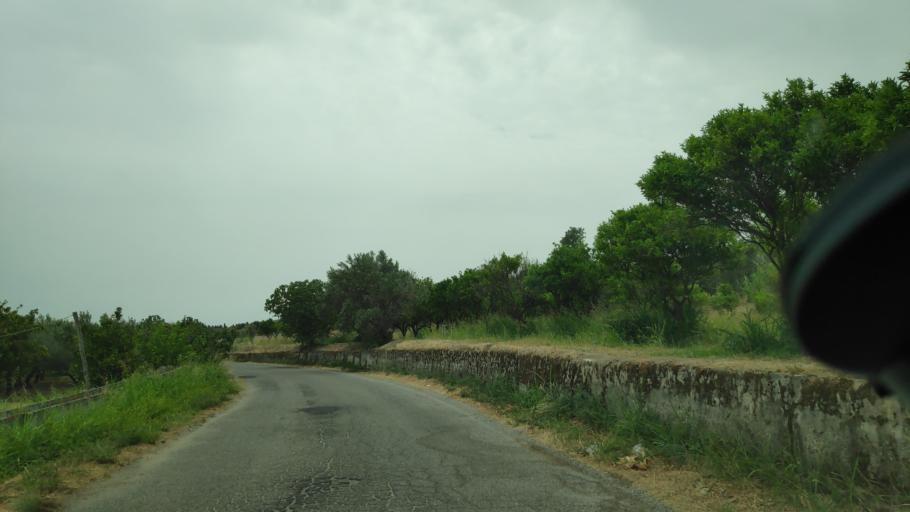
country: IT
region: Calabria
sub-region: Provincia di Catanzaro
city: Martelli-Laganosa
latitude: 38.6660
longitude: 16.5259
